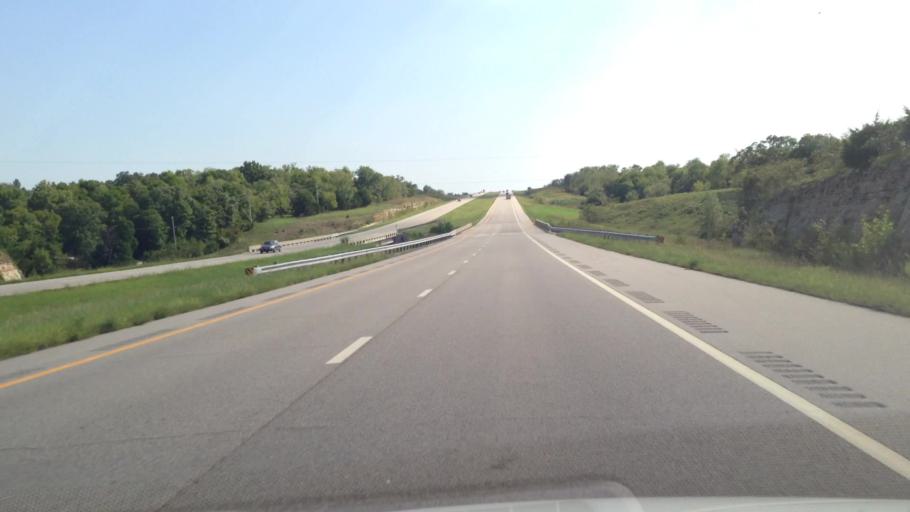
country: US
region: Kansas
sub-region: Linn County
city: La Cygne
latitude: 38.4341
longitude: -94.6871
